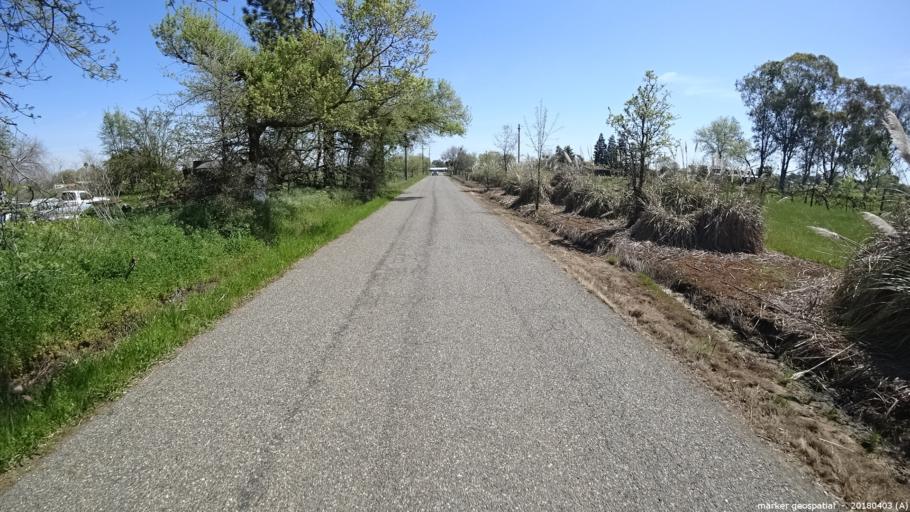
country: US
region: California
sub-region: Sacramento County
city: Wilton
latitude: 38.3952
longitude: -121.2764
